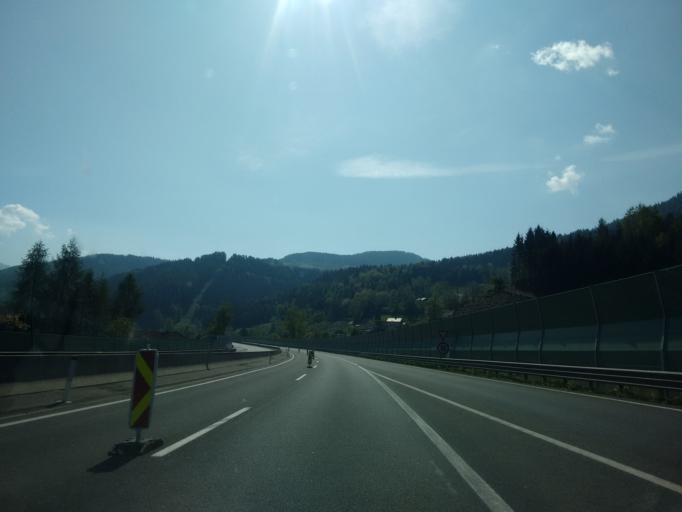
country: AT
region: Styria
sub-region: Politischer Bezirk Bruck-Muerzzuschlag
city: Oberaich
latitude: 47.3989
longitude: 15.2277
